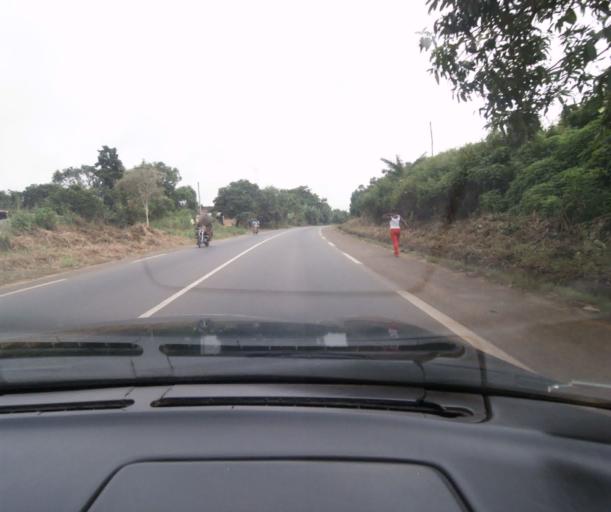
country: CM
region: Centre
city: Obala
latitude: 4.0959
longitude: 11.5384
